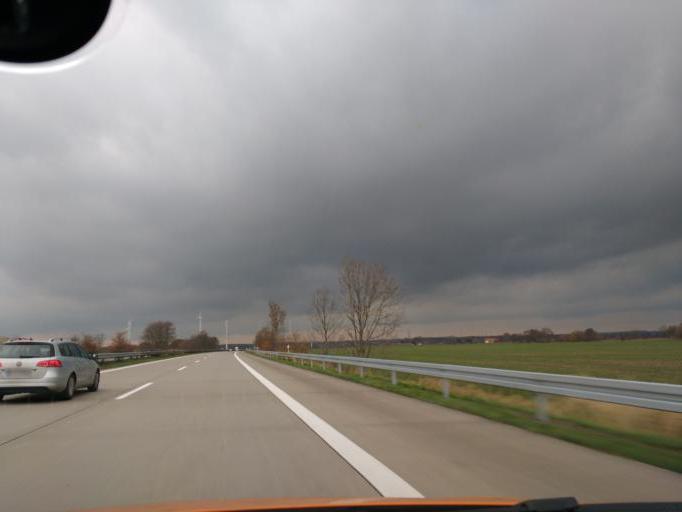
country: DE
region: Brandenburg
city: Heiligengrabe
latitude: 53.1743
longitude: 12.3189
